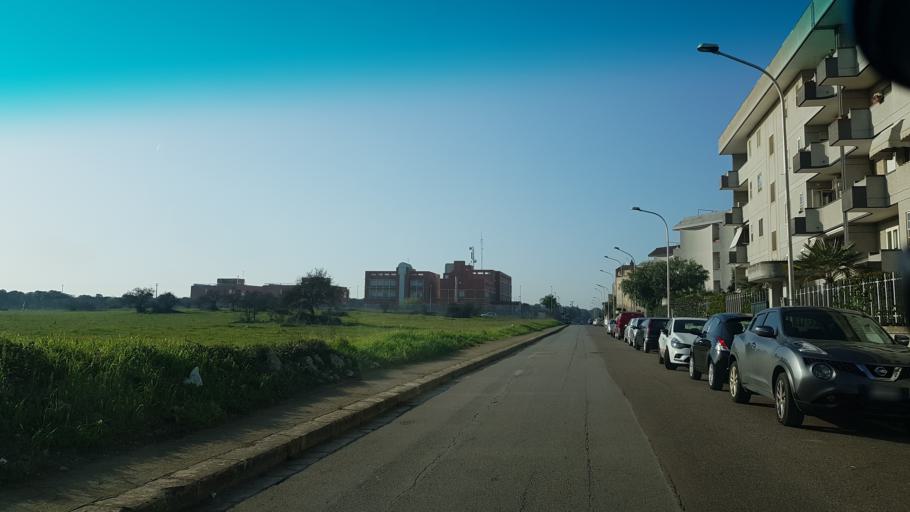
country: IT
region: Apulia
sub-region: Provincia di Brindisi
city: San Vito dei Normanni
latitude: 40.6617
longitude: 17.6969
